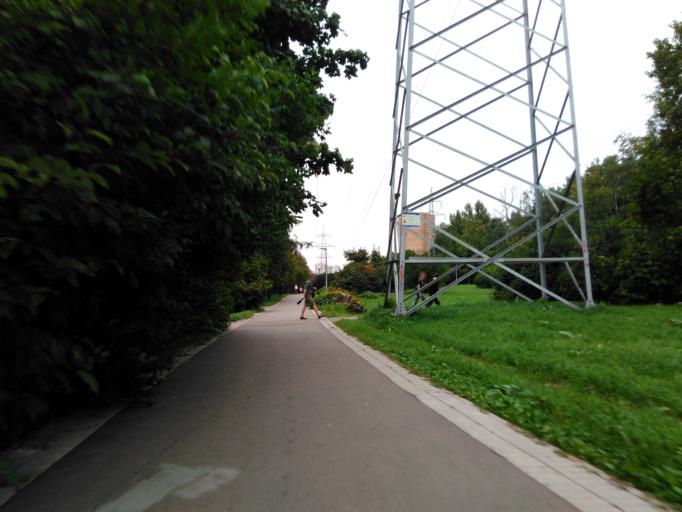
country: RU
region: Moscow
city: Zyuzino
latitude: 55.6503
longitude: 37.5848
